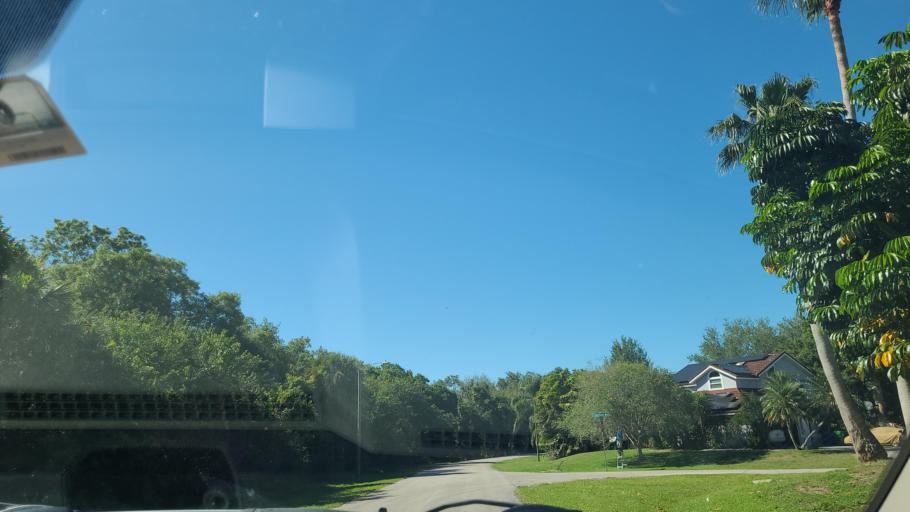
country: US
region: Florida
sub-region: Indian River County
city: Sebastian
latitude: 27.7642
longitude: -80.5017
